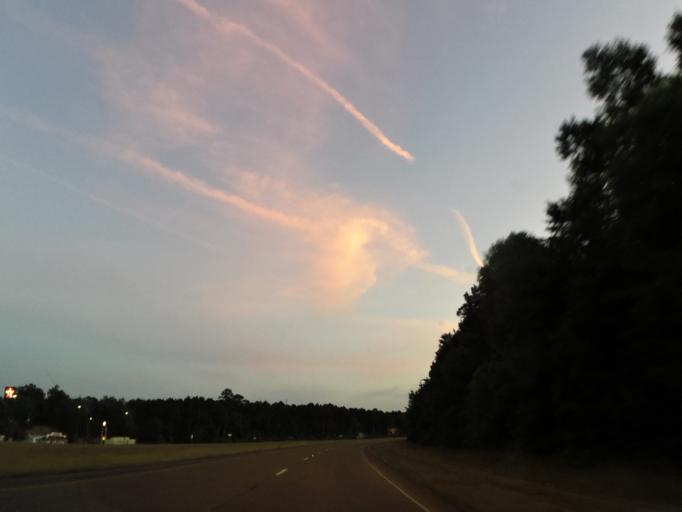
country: US
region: Mississippi
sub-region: Lauderdale County
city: Meridian Station
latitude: 32.5215
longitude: -88.5160
